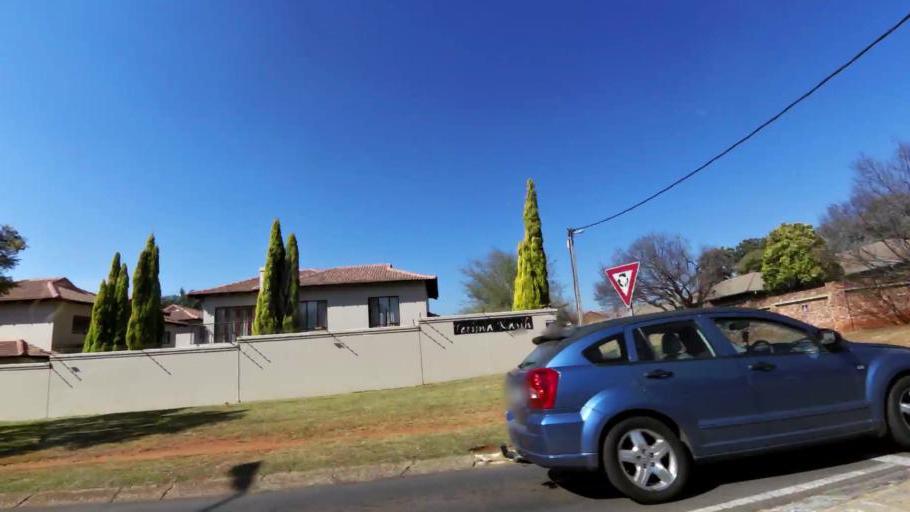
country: ZA
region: Gauteng
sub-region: City of Johannesburg Metropolitan Municipality
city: Roodepoort
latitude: -26.1243
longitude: 27.9488
